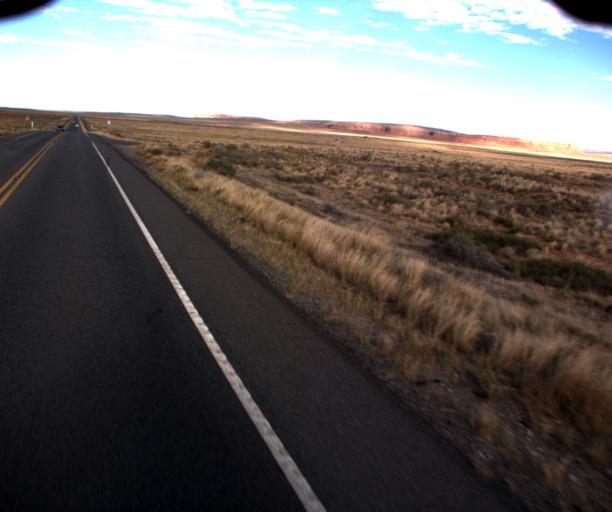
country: US
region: Arizona
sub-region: Apache County
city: Lukachukai
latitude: 36.9387
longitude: -109.2453
